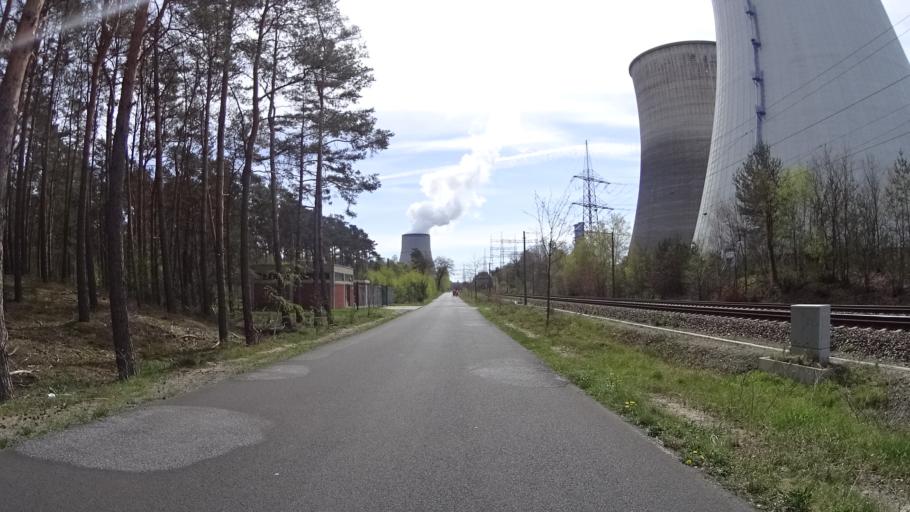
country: DE
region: Lower Saxony
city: Lingen
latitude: 52.4845
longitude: 7.3064
